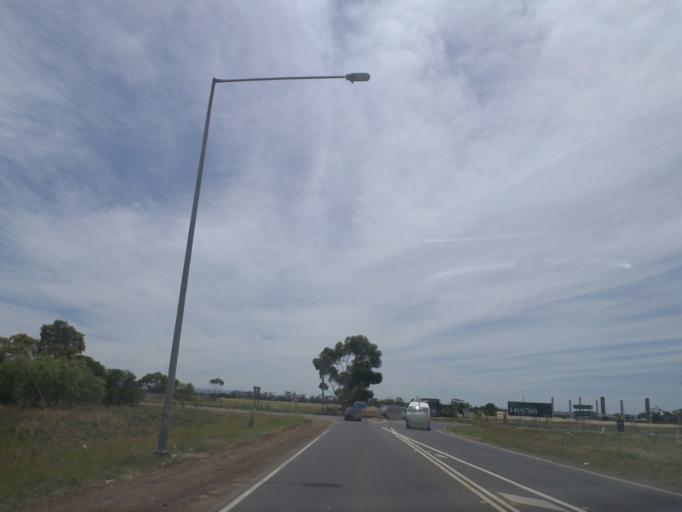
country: AU
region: Victoria
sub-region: Melton
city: Rockbank
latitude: -37.7415
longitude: 144.7010
